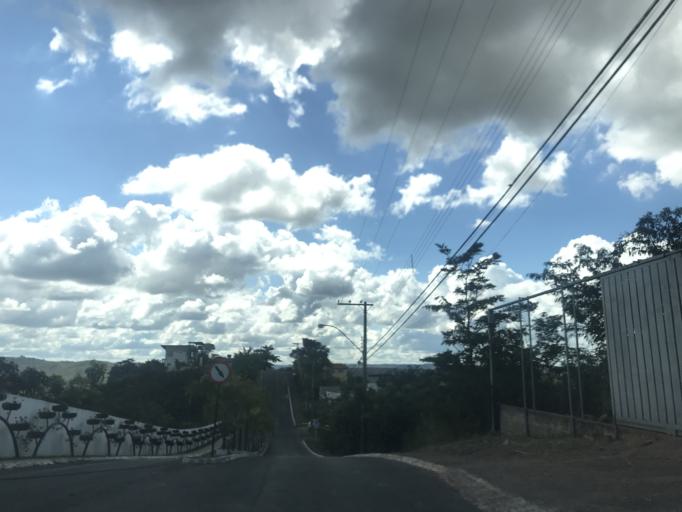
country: BR
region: Federal District
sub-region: Brasilia
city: Brasilia
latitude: -15.8685
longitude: -47.7587
